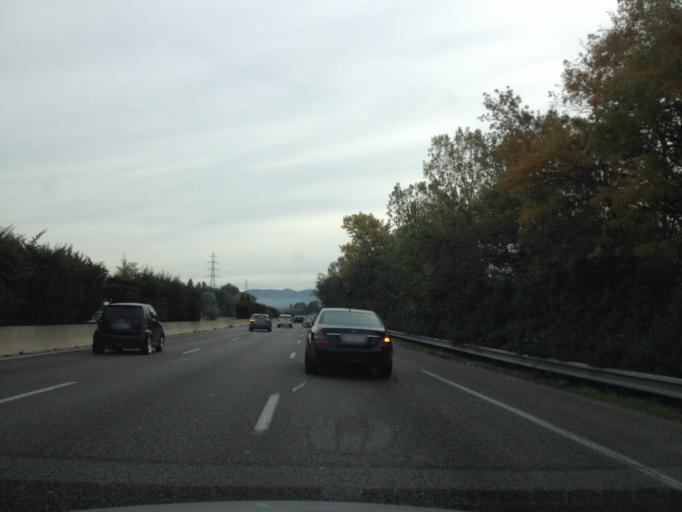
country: FR
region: Provence-Alpes-Cote d'Azur
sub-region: Departement des Bouches-du-Rhone
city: La Penne-sur-Huveaune
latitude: 43.2868
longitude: 5.5066
